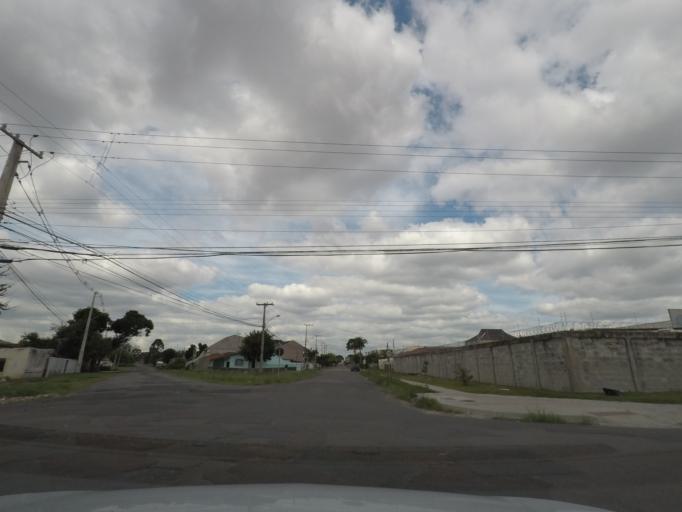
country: BR
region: Parana
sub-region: Sao Jose Dos Pinhais
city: Sao Jose dos Pinhais
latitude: -25.4902
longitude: -49.2377
